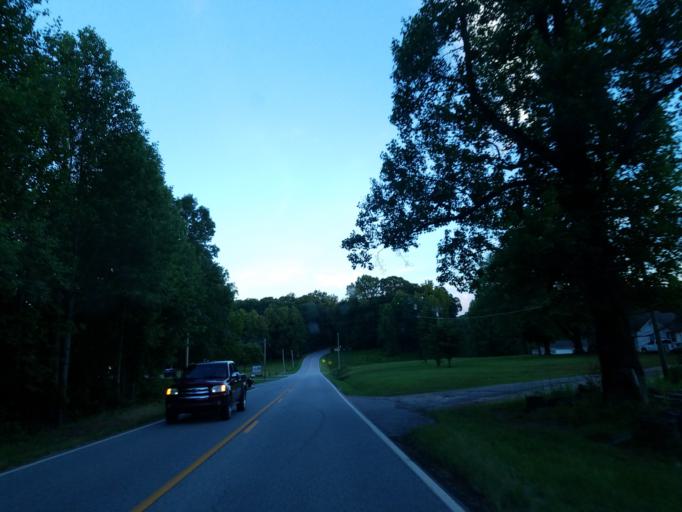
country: US
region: Georgia
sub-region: Lumpkin County
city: Dahlonega
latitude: 34.5765
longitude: -83.9681
